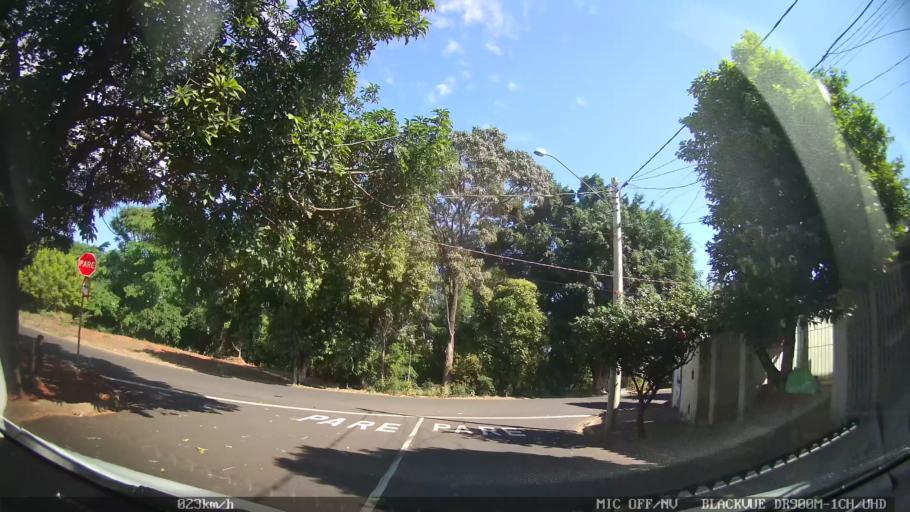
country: BR
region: Sao Paulo
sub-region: Santa Barbara D'Oeste
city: Santa Barbara d'Oeste
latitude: -22.7431
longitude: -47.3871
